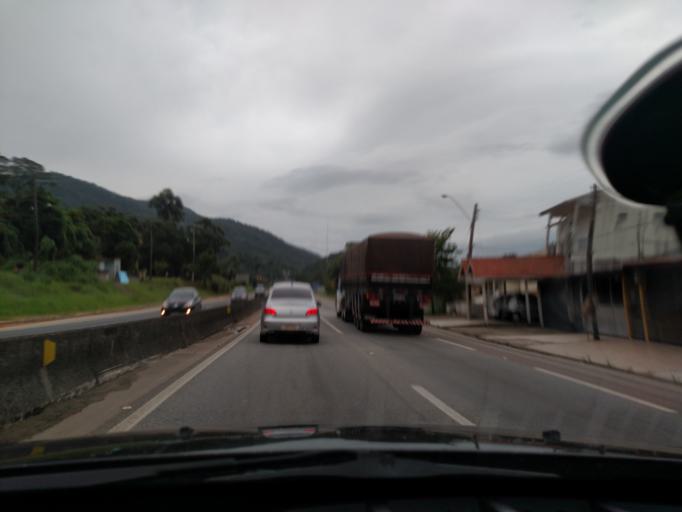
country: BR
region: Santa Catarina
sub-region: Biguacu
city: Biguacu
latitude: -27.4744
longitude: -48.6408
